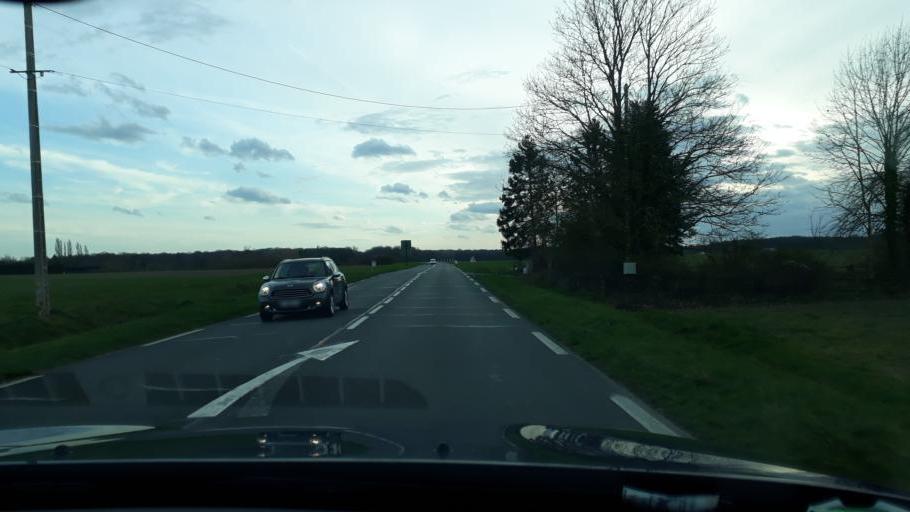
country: FR
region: Centre
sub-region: Departement du Loiret
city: Chilleurs-aux-Bois
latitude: 48.0641
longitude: 2.1308
